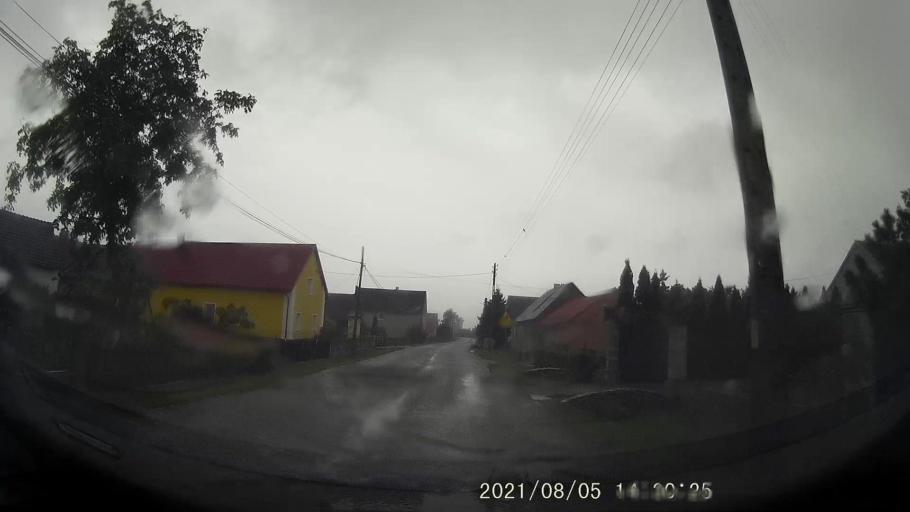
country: PL
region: Opole Voivodeship
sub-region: Powiat nyski
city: Korfantow
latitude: 50.4838
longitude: 17.5556
